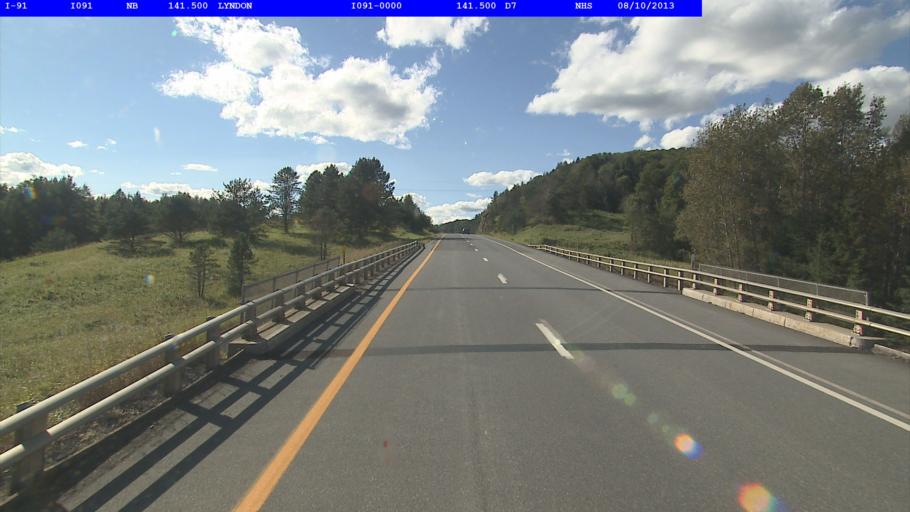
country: US
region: Vermont
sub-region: Caledonia County
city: Lyndonville
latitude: 44.5727
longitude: -72.0416
